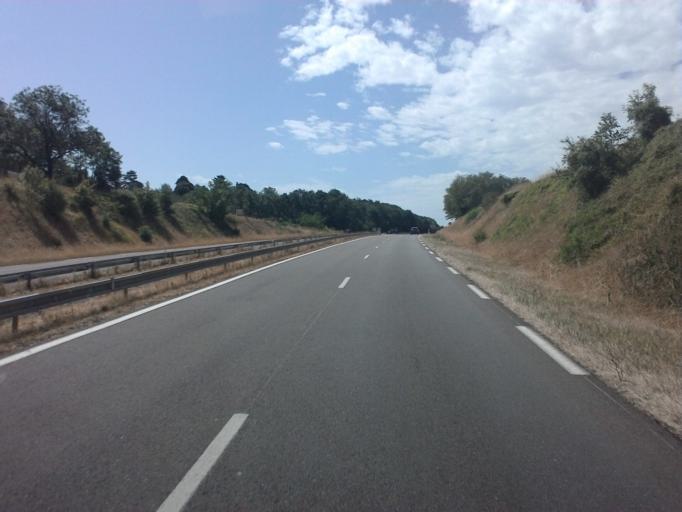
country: FR
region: Franche-Comte
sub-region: Departement du Jura
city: Cousance
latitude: 46.5509
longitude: 5.4032
